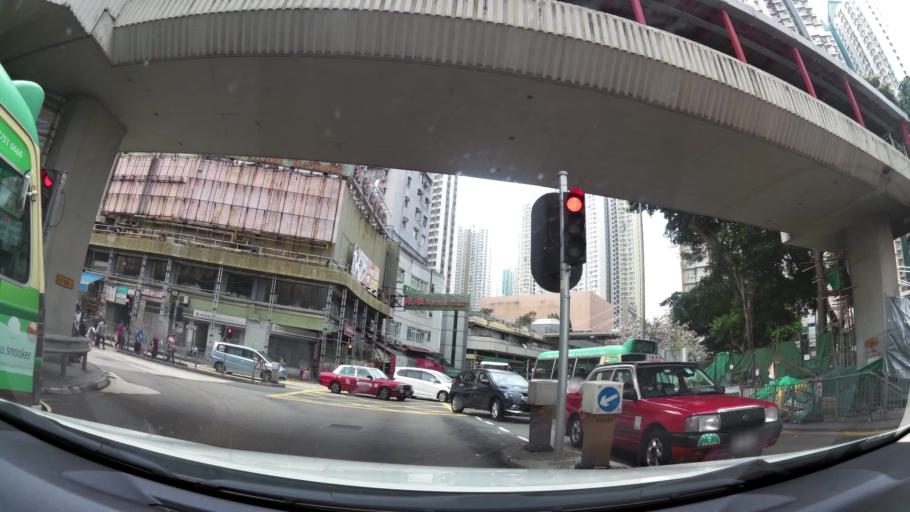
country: HK
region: Kowloon City
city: Kowloon
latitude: 22.3228
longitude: 114.2165
